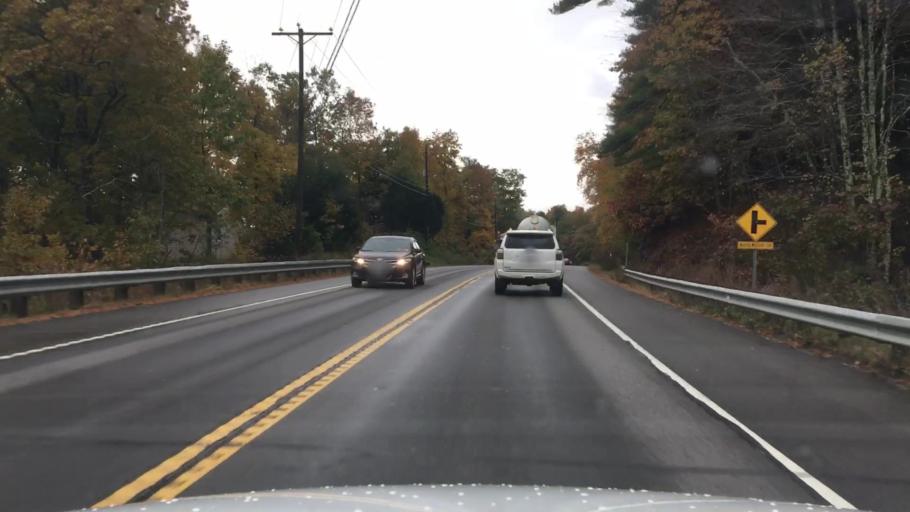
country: US
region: New Hampshire
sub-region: Strafford County
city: Lee
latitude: 43.1374
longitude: -71.0161
